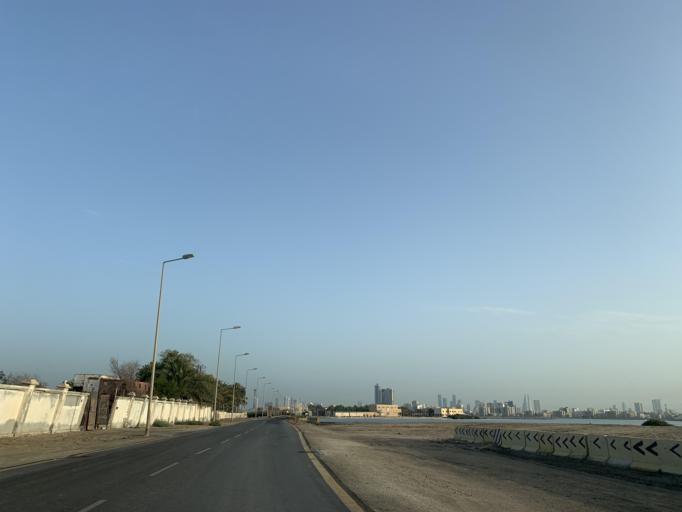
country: BH
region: Manama
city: Manama
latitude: 26.1853
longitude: 50.5873
